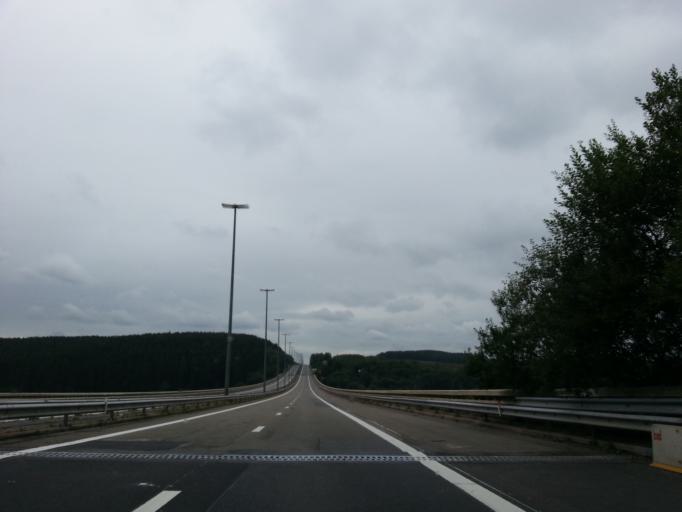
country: BE
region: Wallonia
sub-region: Province de Liege
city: Saint-Vith
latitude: 50.2614
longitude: 6.1529
